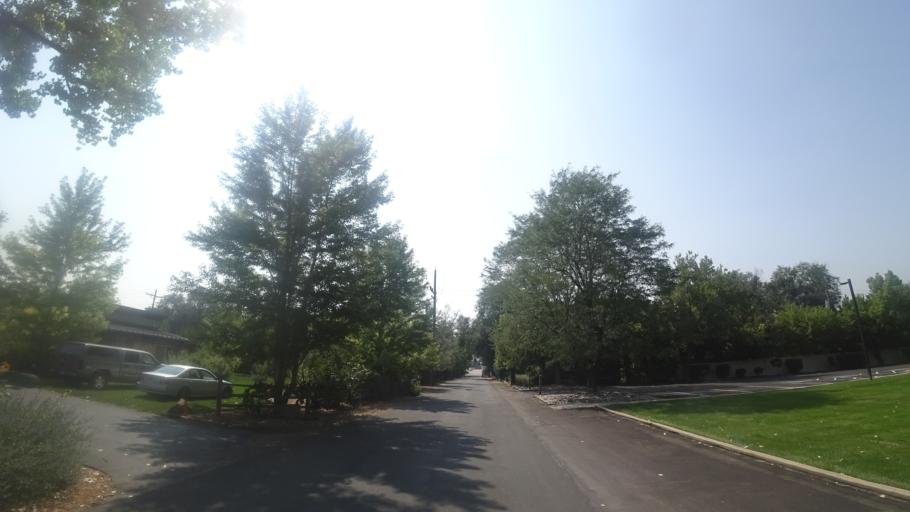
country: US
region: Colorado
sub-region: Arapahoe County
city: Englewood
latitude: 39.6332
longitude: -104.9767
